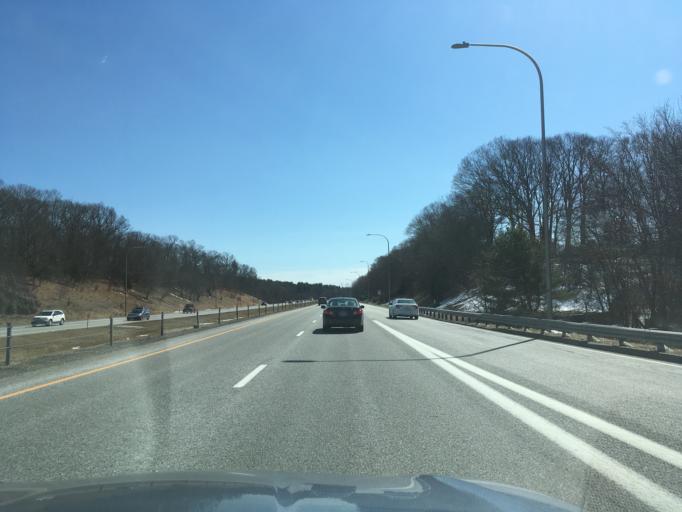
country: US
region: Rhode Island
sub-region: Kent County
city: East Greenwich
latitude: 41.6256
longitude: -71.4870
